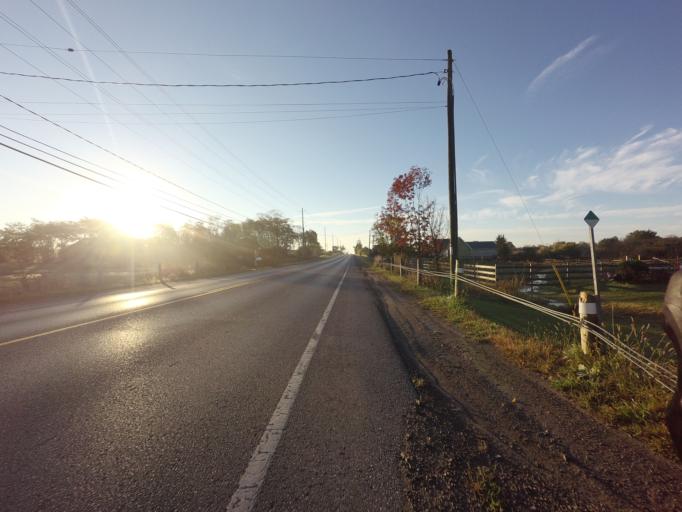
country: CA
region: Ontario
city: Quinte West
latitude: 44.0218
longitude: -77.5434
